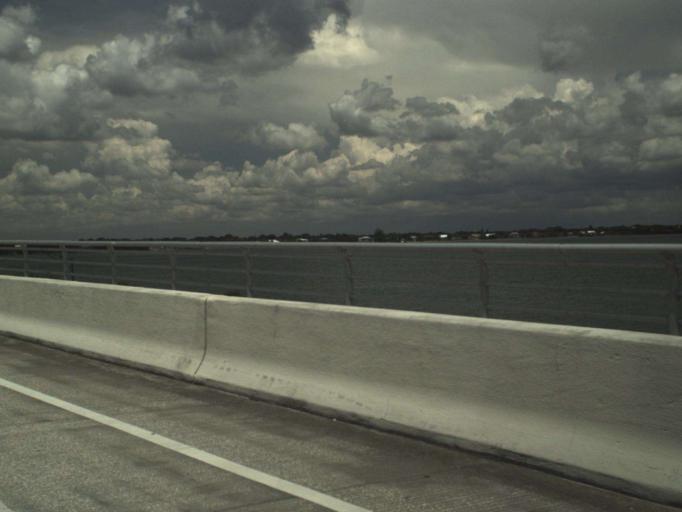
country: US
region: Florida
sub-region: Martin County
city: Sewall's Point
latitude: 27.2091
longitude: -80.1872
